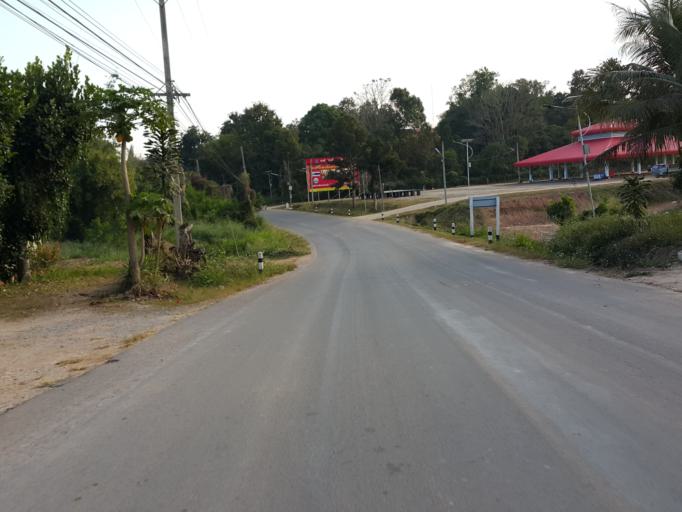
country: TH
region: Lamphun
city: Thung Hua Chang
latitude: 18.0064
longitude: 99.0274
